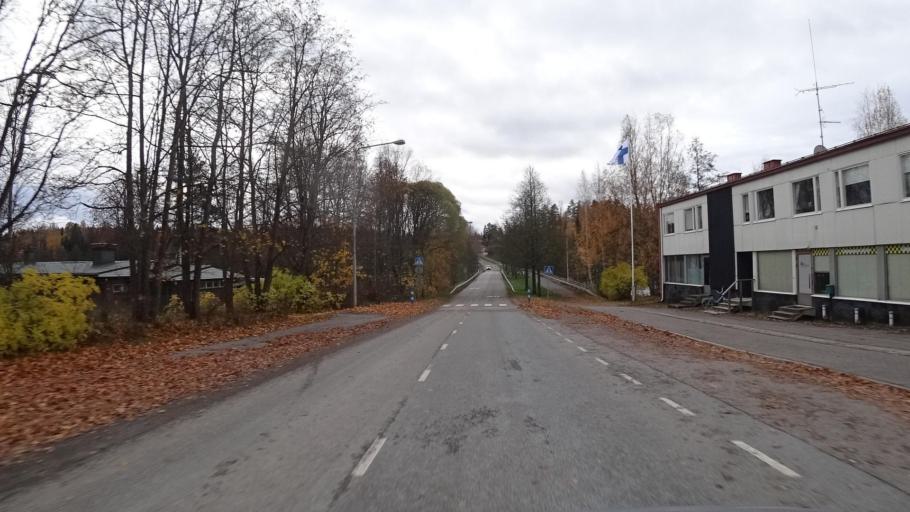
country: FI
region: Central Finland
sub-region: Joutsa
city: Joutsa
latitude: 61.7387
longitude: 26.1116
